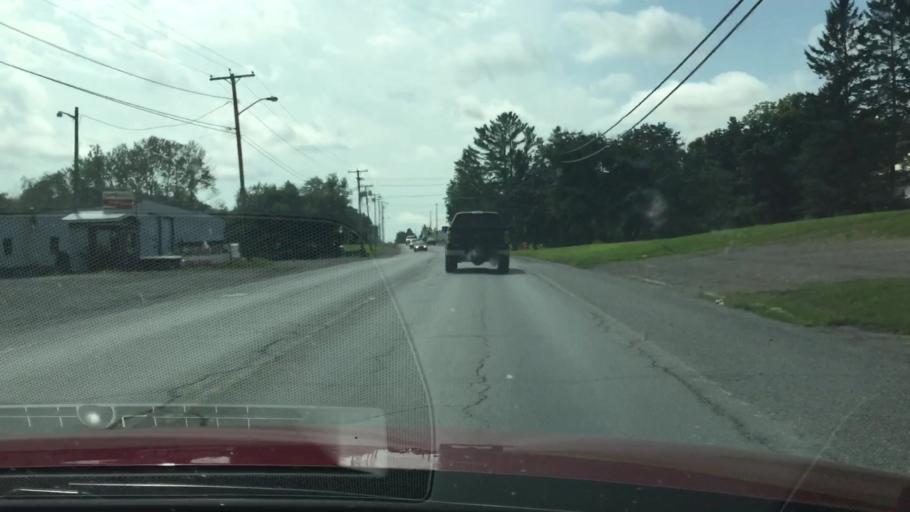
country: US
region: Maine
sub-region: Aroostook County
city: Easton
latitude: 46.5093
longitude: -67.8684
